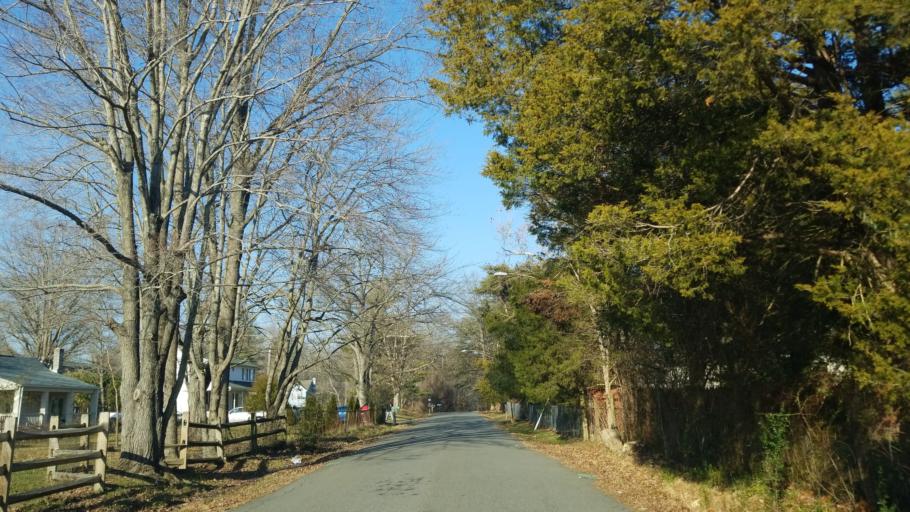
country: US
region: Virginia
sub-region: Fairfax County
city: Fairfax Station
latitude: 38.8286
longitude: -77.3711
